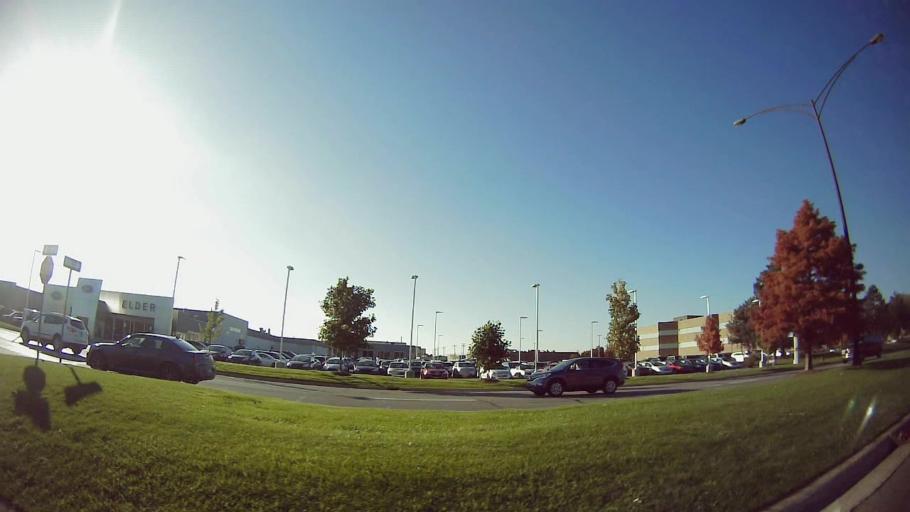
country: US
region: Michigan
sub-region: Oakland County
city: Clawson
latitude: 42.5425
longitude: -83.1073
